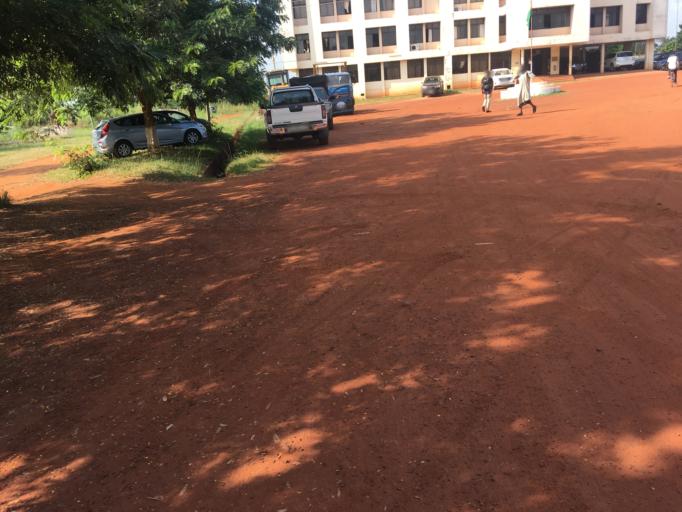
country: GH
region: Brong-Ahafo
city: Techiman
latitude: 7.5844
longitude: -1.9266
